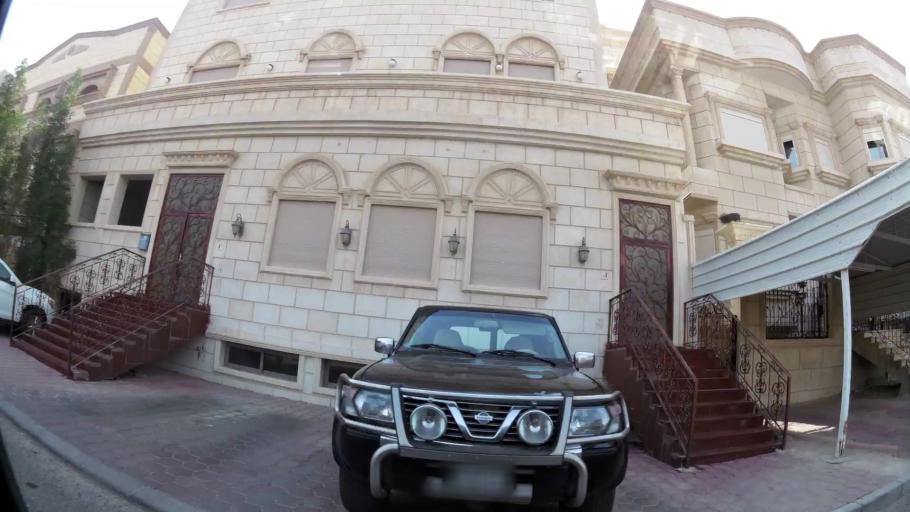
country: KW
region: Muhafazat al Jahra'
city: Al Jahra'
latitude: 29.3070
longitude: 47.6895
